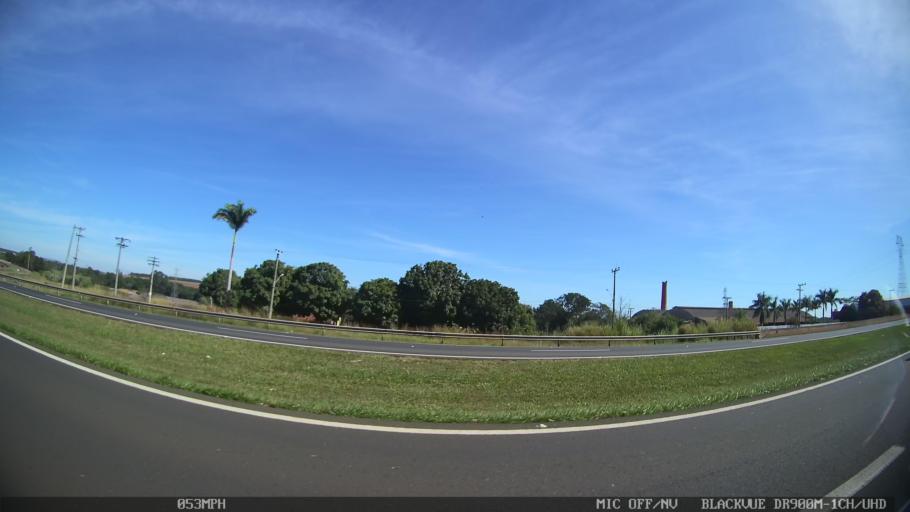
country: BR
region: Sao Paulo
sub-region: Porto Ferreira
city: Porto Ferreira
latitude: -21.8319
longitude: -47.4951
